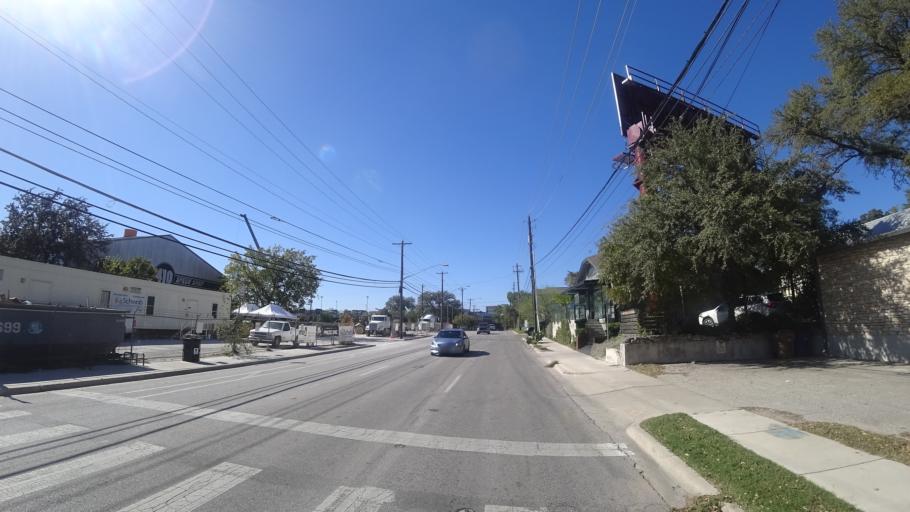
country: US
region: Texas
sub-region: Travis County
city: Austin
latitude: 30.2728
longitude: -97.7609
